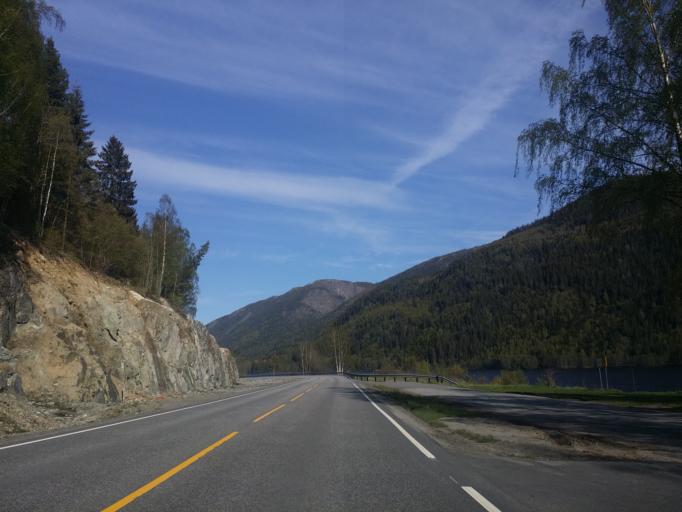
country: NO
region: Telemark
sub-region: Seljord
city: Seljord
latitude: 59.6054
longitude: 8.7211
